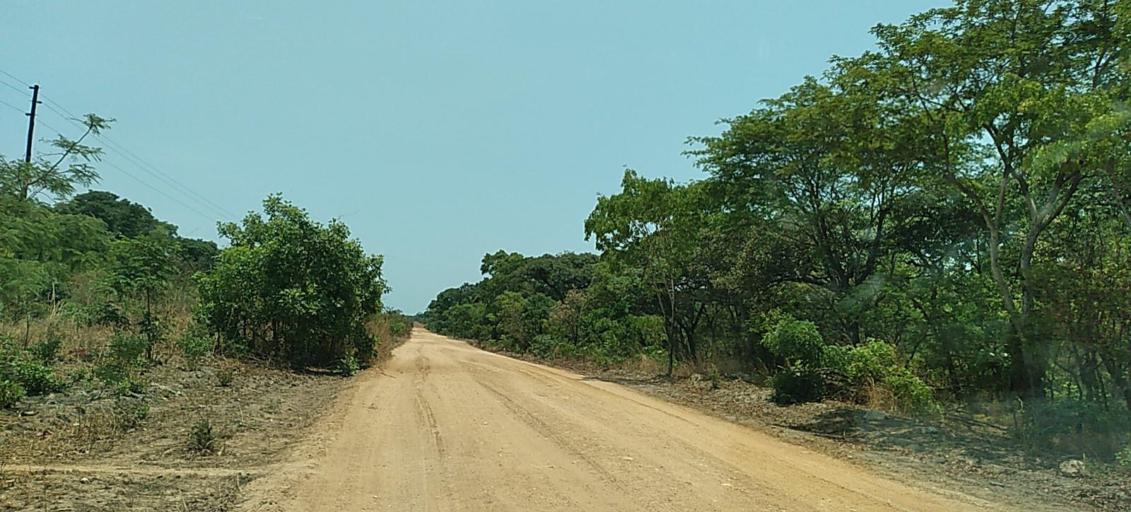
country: ZM
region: Copperbelt
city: Mpongwe
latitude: -13.8009
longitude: 27.8596
